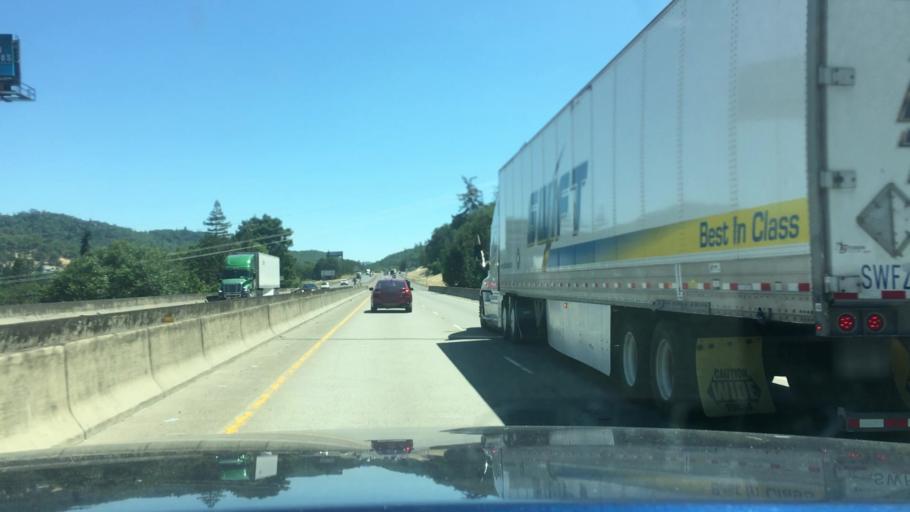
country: US
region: Oregon
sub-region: Douglas County
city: Roseburg North
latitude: 43.2809
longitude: -123.3559
